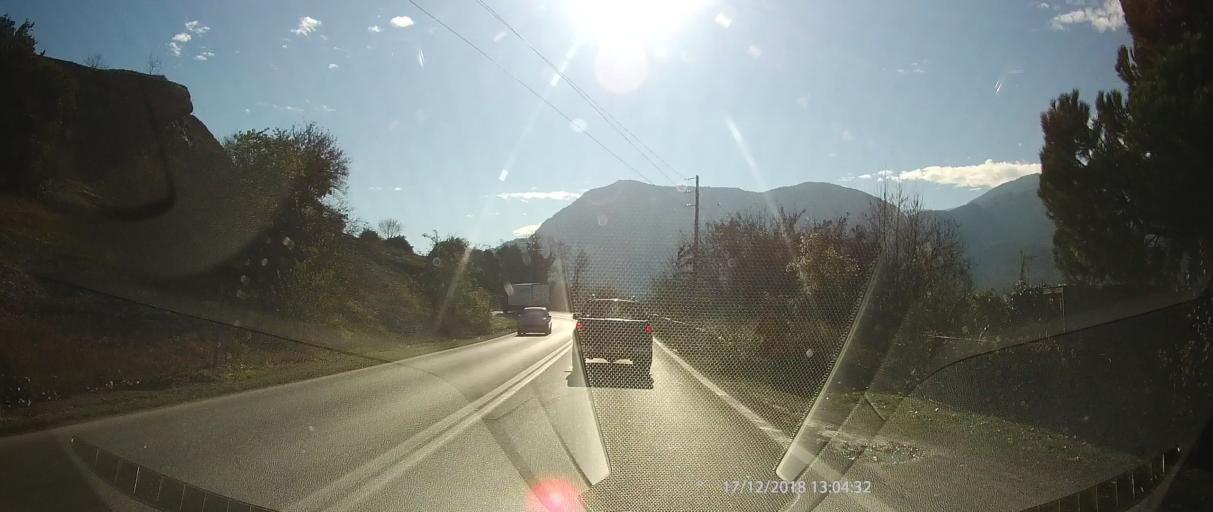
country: GR
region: Thessaly
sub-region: Trikala
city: Kastraki
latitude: 39.7046
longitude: 21.6117
